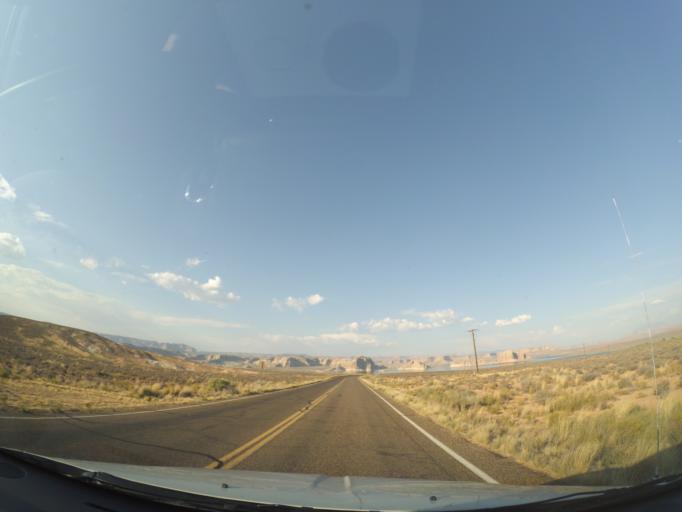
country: US
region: Arizona
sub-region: Coconino County
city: Page
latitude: 36.9903
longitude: -111.5115
